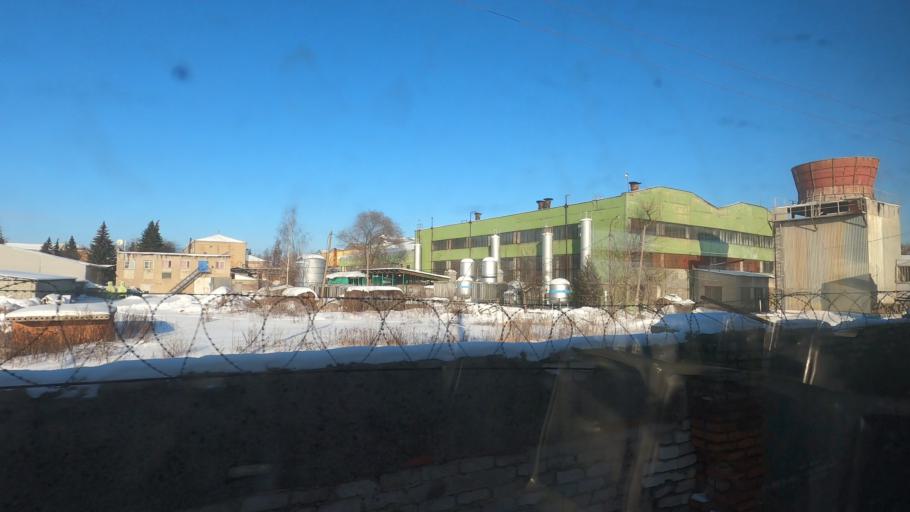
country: RU
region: Moskovskaya
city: Pavlovskiy Posad
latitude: 55.7743
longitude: 38.6936
